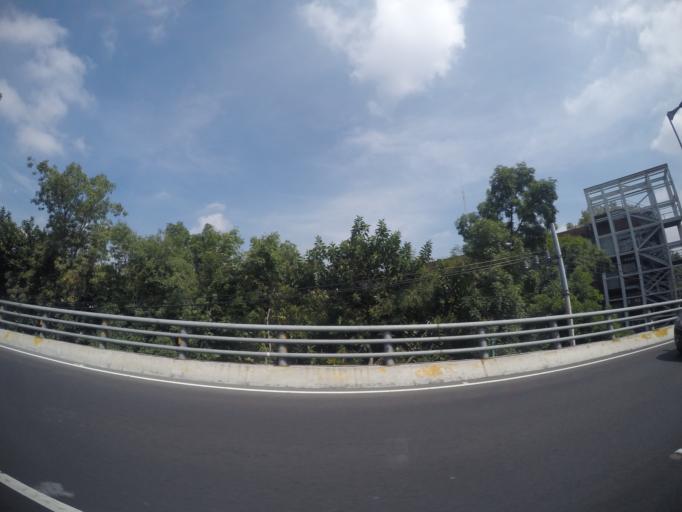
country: MX
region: Mexico City
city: Magdalena Contreras
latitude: 19.3330
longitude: -99.2098
